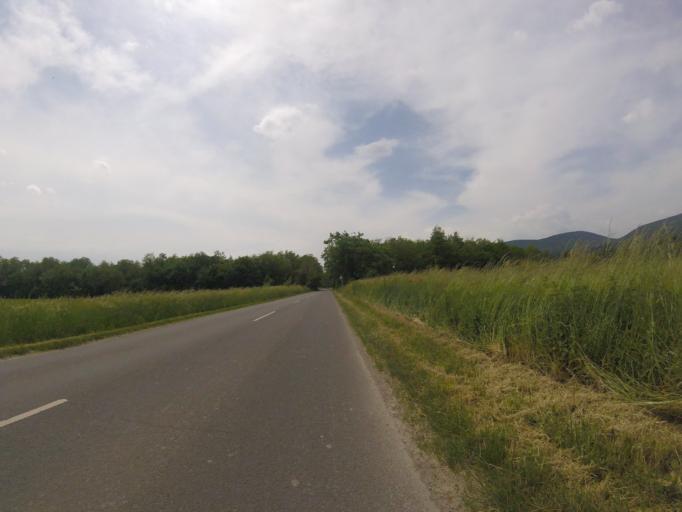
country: HU
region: Pest
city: Tahitotfalu
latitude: 47.7313
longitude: 19.1023
